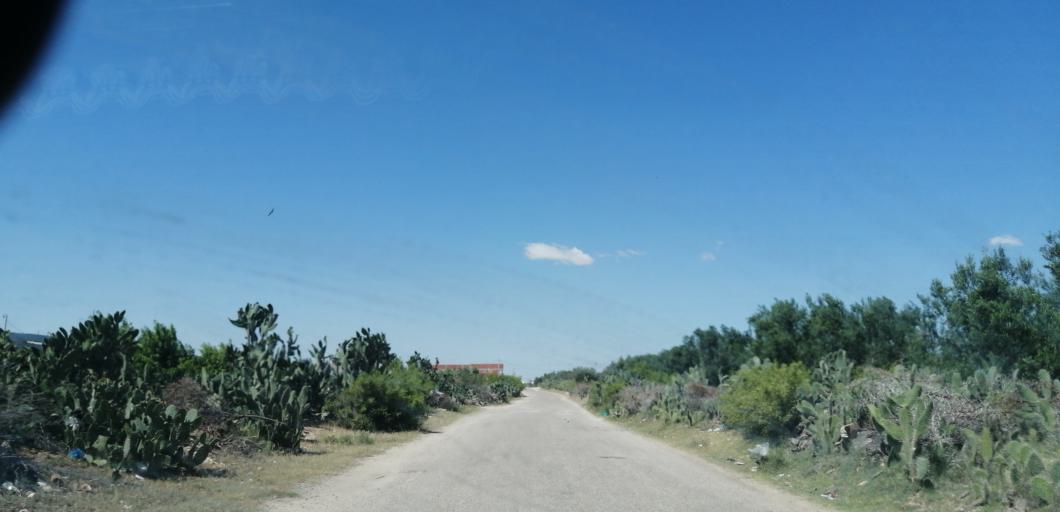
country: TN
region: Al Qayrawan
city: Kairouan
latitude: 35.6293
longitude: 9.9372
